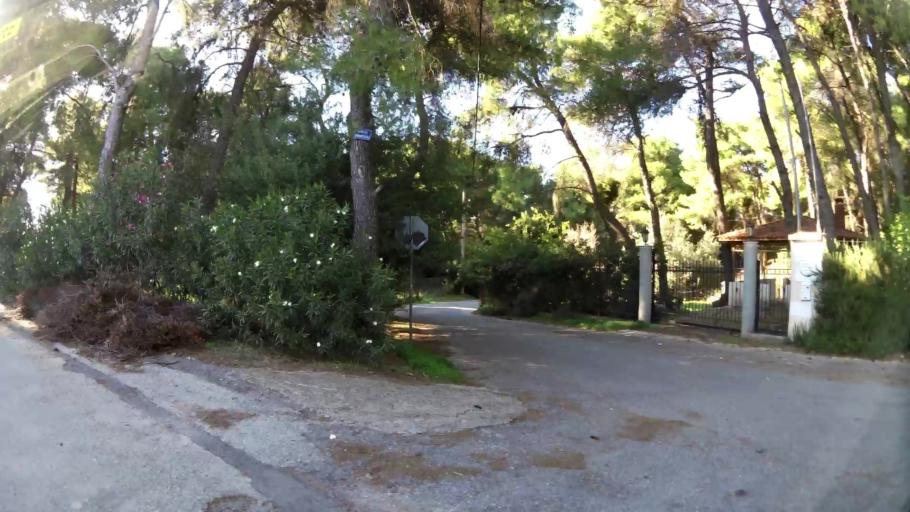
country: GR
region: Attica
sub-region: Nomarchia Anatolikis Attikis
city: Anoixi
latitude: 38.1257
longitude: 23.8552
